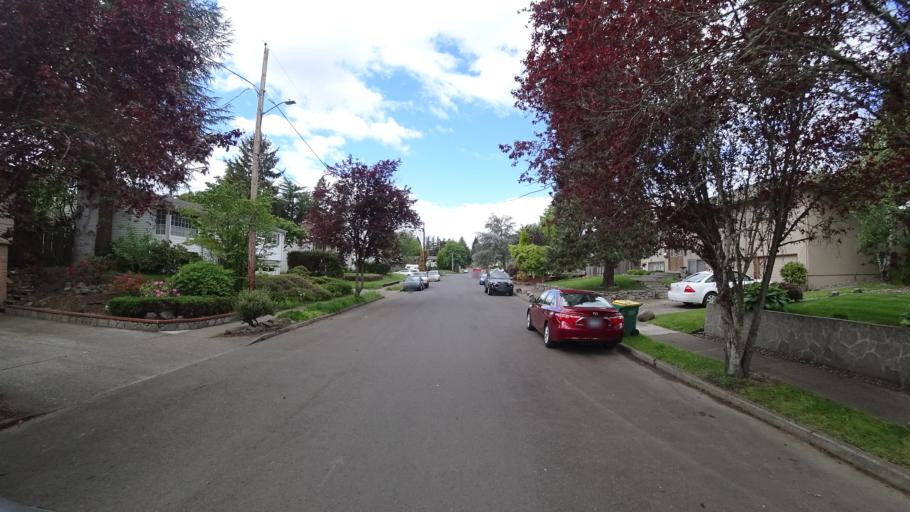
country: US
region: Oregon
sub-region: Washington County
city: Beaverton
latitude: 45.4664
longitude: -122.7981
